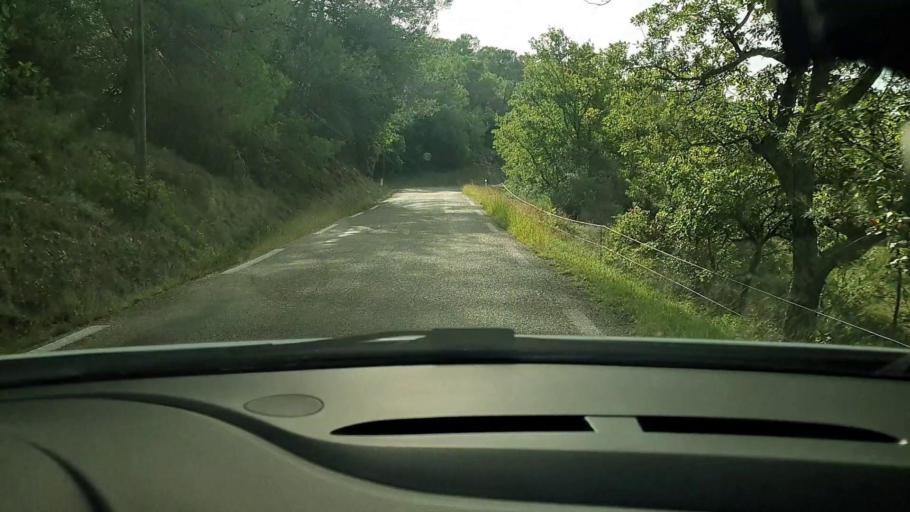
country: FR
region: Languedoc-Roussillon
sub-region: Departement du Gard
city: Montaren-et-Saint-Mediers
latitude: 44.0835
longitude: 4.3852
